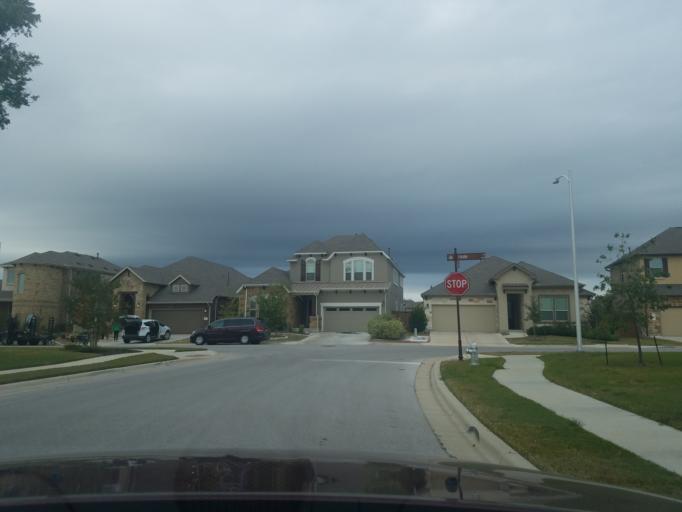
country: US
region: Texas
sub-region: Williamson County
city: Cedar Park
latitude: 30.4888
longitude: -97.7900
